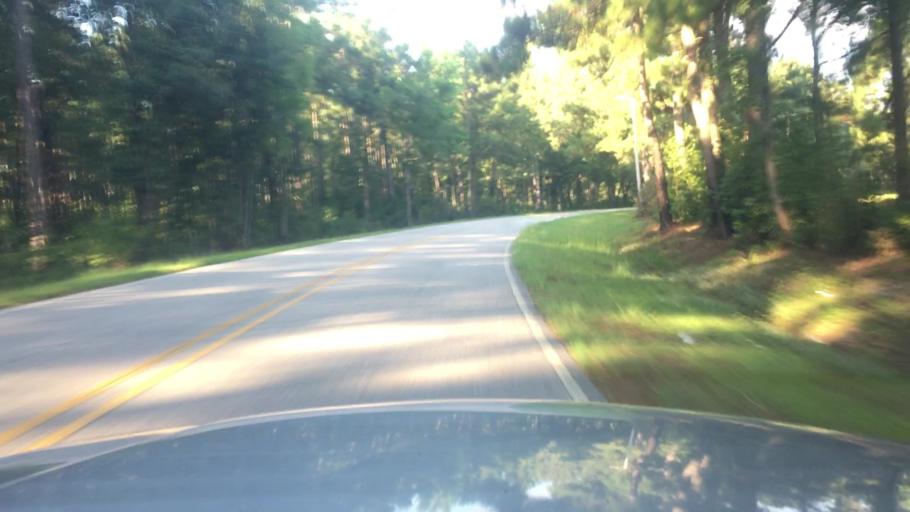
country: US
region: North Carolina
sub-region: Harnett County
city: Walkertown
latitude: 35.2276
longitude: -78.8781
